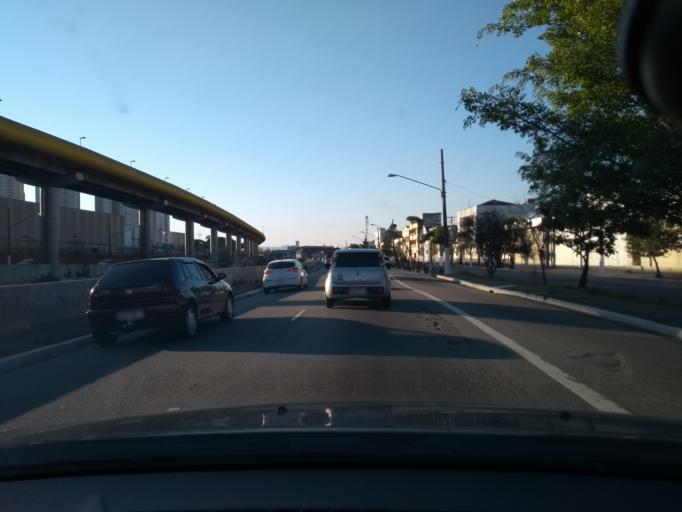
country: BR
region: Sao Paulo
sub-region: Sao Paulo
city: Sao Paulo
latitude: -23.5794
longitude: -46.5994
